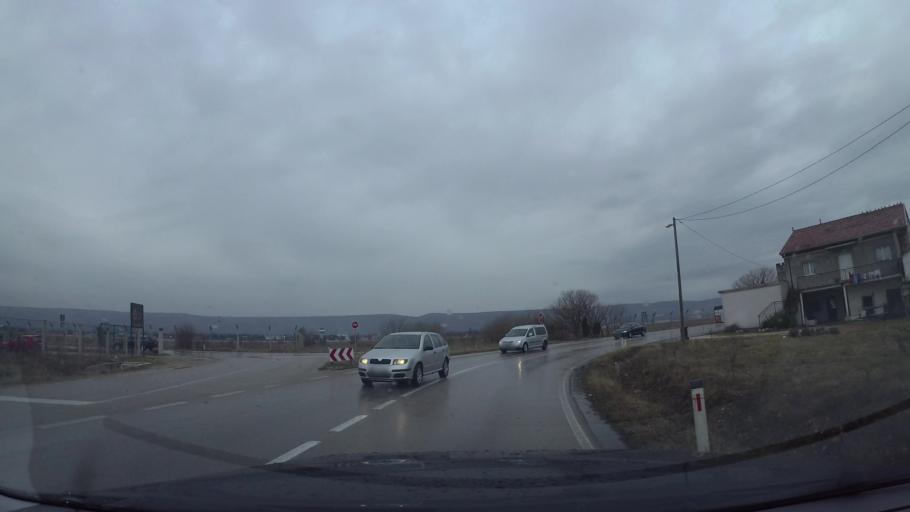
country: BA
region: Federation of Bosnia and Herzegovina
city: Blagaj
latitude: 43.2891
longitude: 17.8487
